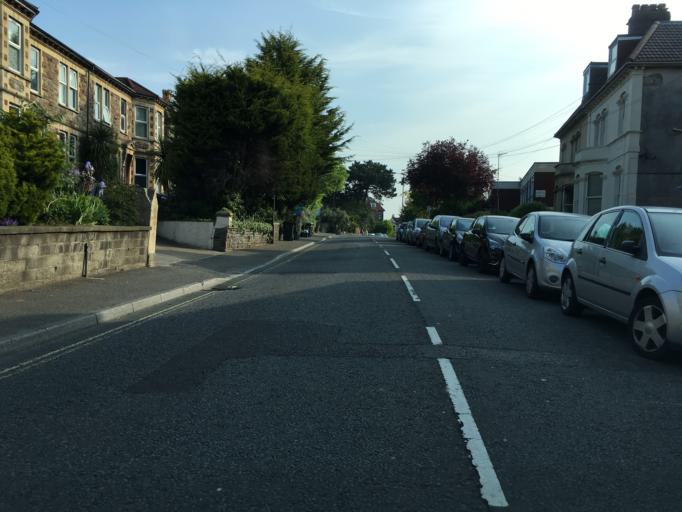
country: GB
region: England
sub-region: Bristol
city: Bristol
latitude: 51.4696
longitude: -2.5855
